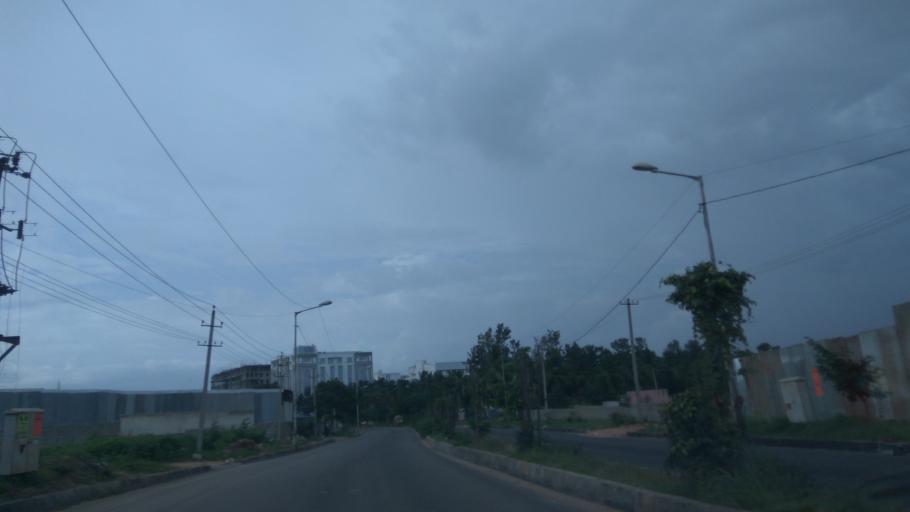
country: IN
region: Karnataka
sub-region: Bangalore Urban
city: Yelahanka
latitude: 13.1109
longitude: 77.6338
